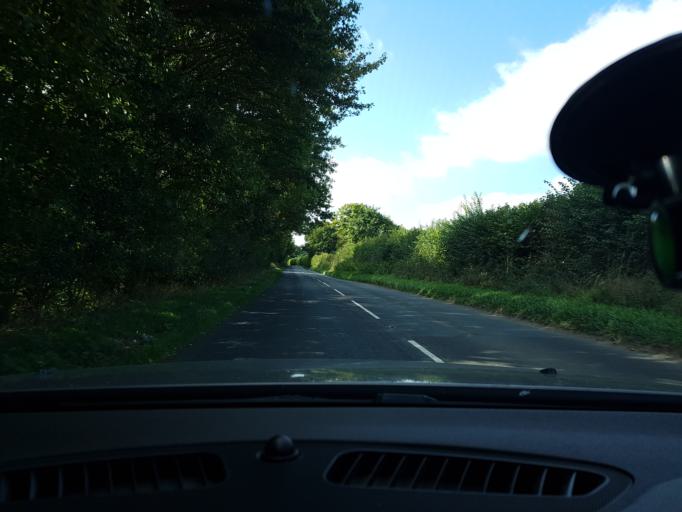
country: GB
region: England
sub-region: Wiltshire
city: Chilton Foliat
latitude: 51.4359
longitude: -1.5592
